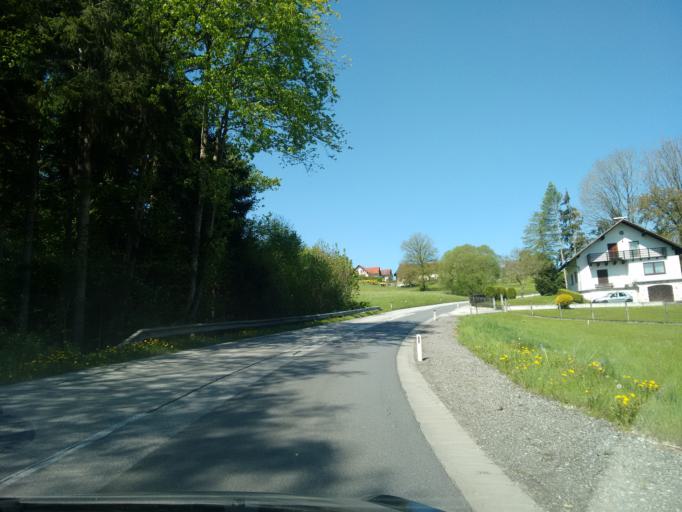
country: AT
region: Upper Austria
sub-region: Politischer Bezirk Steyr-Land
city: Waldneukirchen
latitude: 47.9926
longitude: 14.2602
